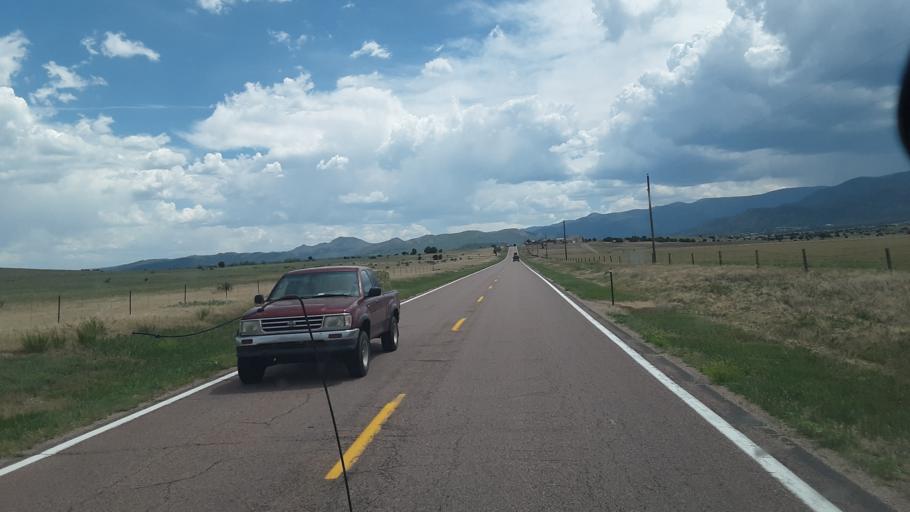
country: US
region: Colorado
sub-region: Fremont County
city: Florence
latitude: 38.2756
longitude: -105.0874
